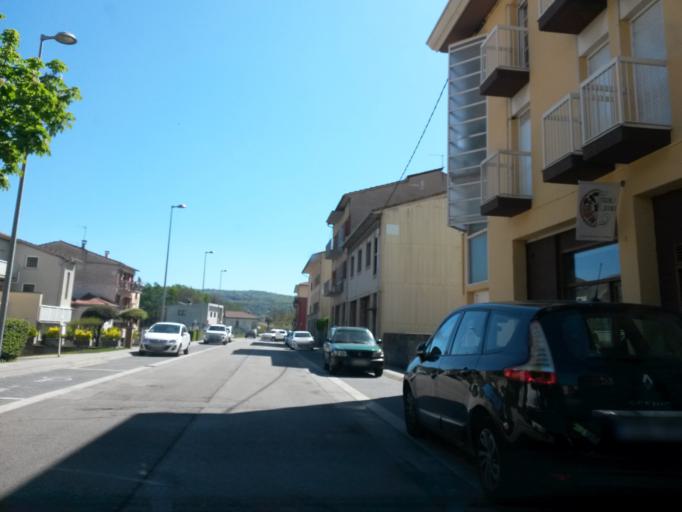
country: ES
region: Catalonia
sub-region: Provincia de Girona
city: Olot
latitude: 42.1692
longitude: 2.4770
